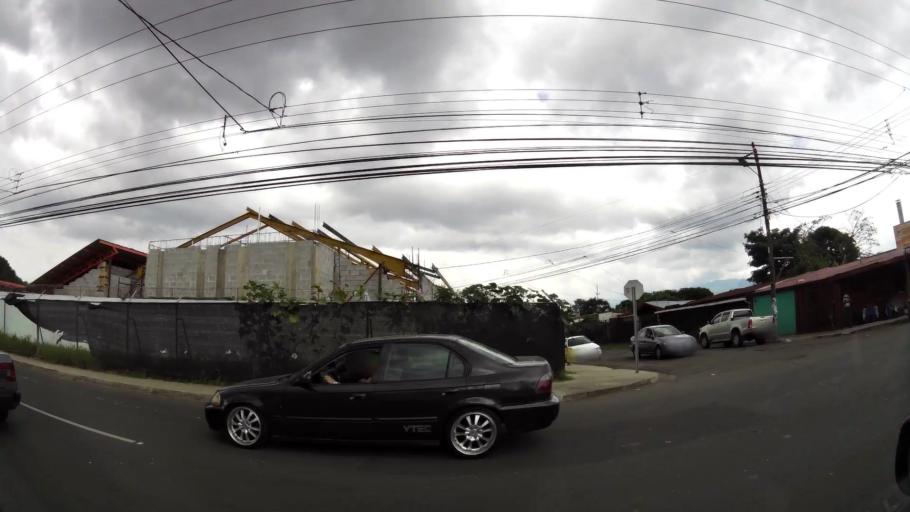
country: CR
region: San Jose
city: Alajuelita
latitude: 9.8951
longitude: -84.0839
